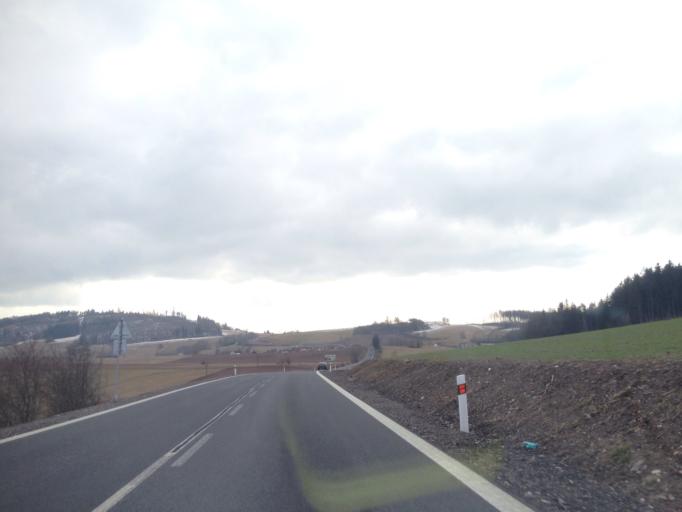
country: CZ
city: Horni Branna
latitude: 50.5808
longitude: 15.5669
